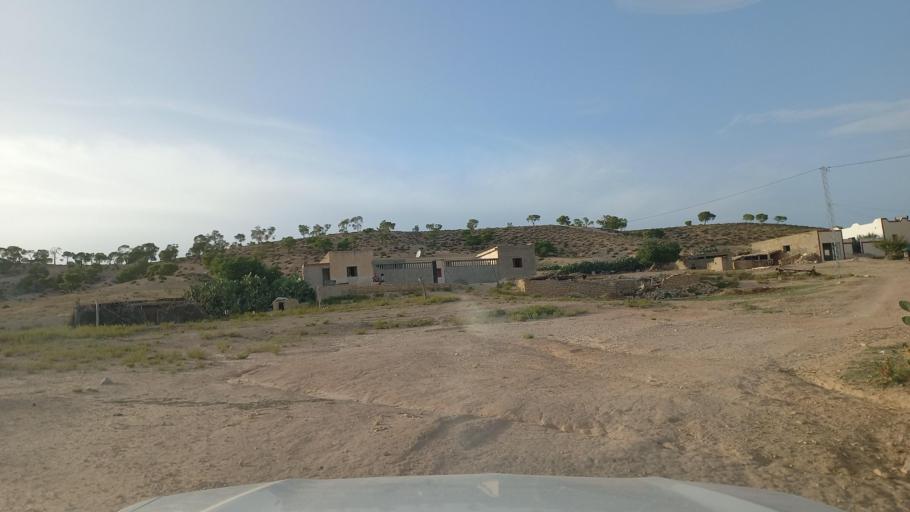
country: TN
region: Al Qasrayn
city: Sbiba
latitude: 35.4061
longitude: 8.8963
